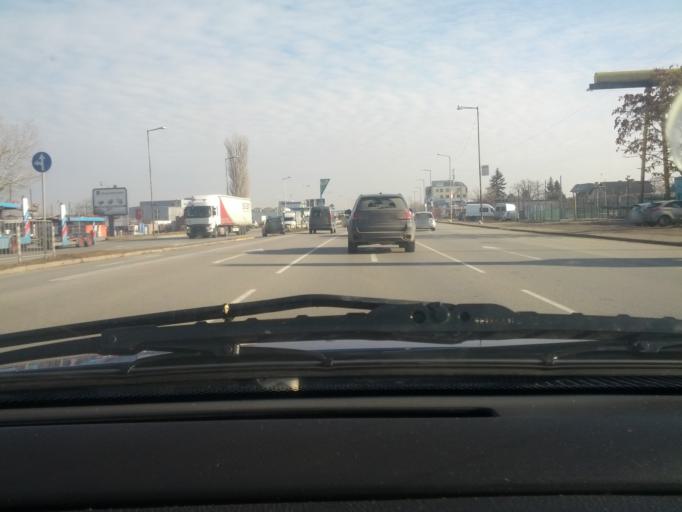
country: BG
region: Sofia-Capital
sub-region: Stolichna Obshtina
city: Sofia
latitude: 42.7093
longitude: 23.4253
